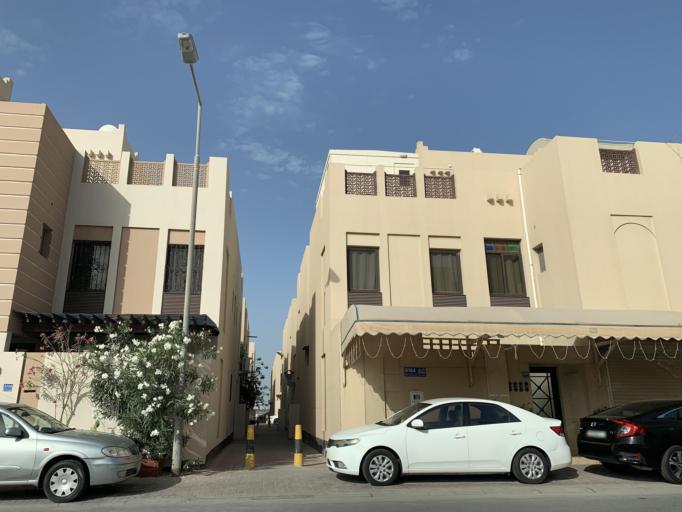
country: BH
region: Manama
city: Manama
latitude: 26.1795
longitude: 50.5894
